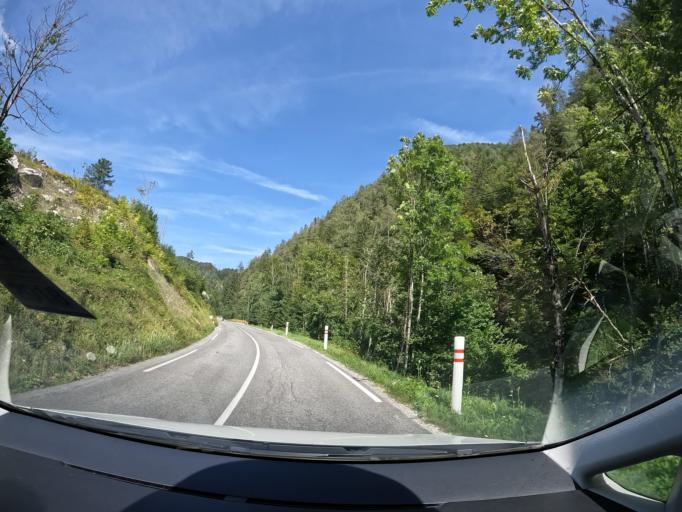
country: SI
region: Zirovnica
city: Zirovnica
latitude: 46.4265
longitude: 14.1336
